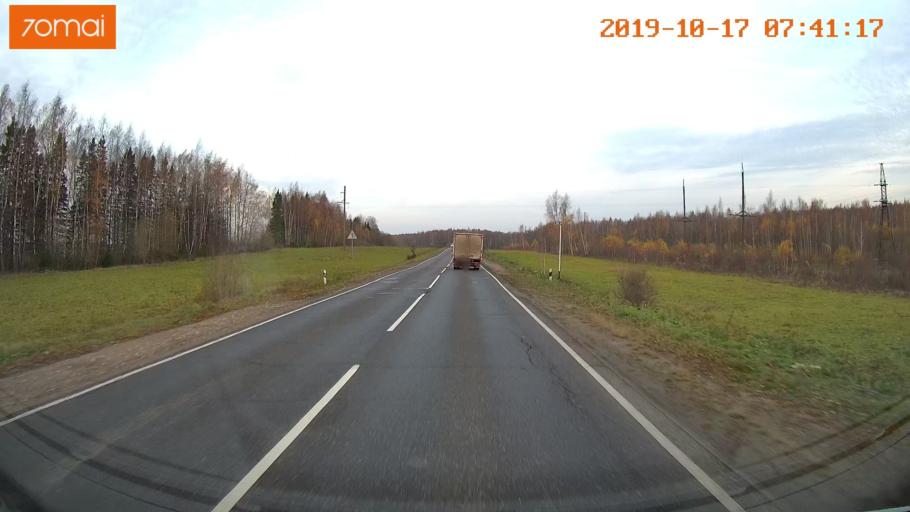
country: RU
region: Vladimir
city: Yur'yev-Pol'skiy
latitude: 56.4808
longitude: 39.8134
